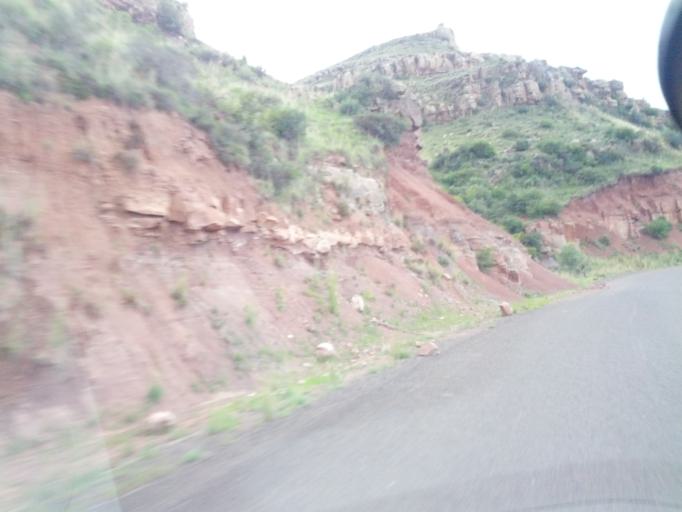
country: LS
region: Qacha's Nek
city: Qacha's Nek
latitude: -30.0590
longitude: 28.5034
